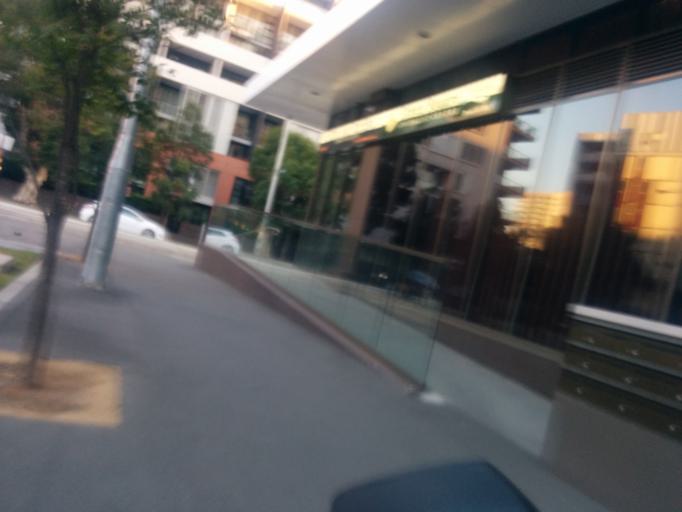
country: AU
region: New South Wales
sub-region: City of Sydney
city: Alexandria
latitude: -33.9030
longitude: 151.2108
